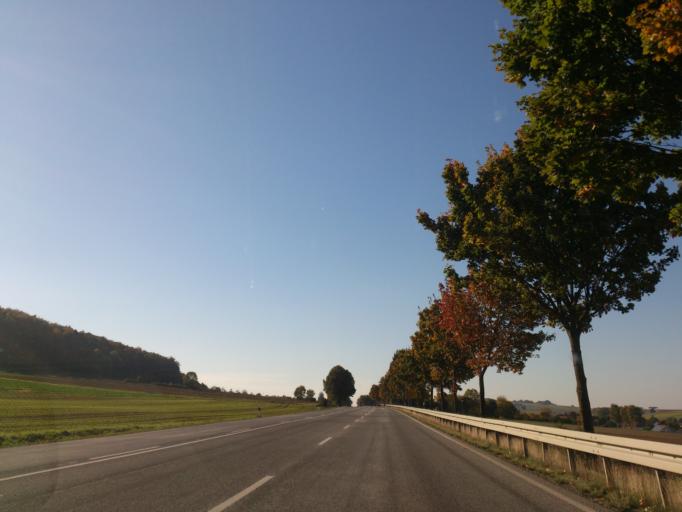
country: DE
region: Hesse
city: Liebenau
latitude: 51.4451
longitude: 9.2660
